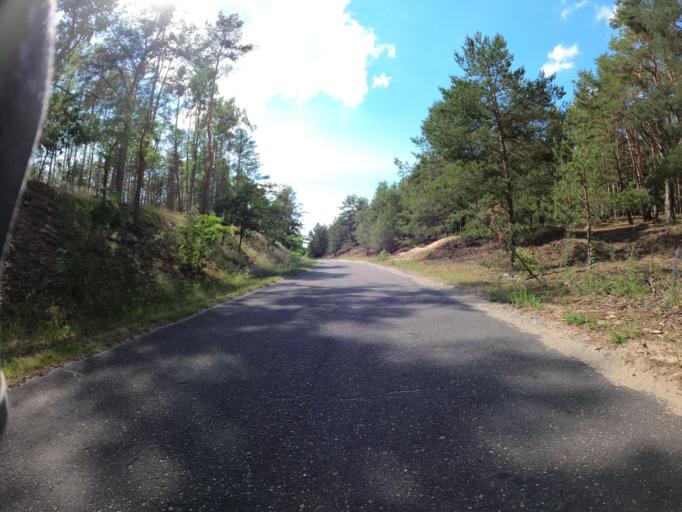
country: DE
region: Brandenburg
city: Neulewin
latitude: 52.7629
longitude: 14.3531
